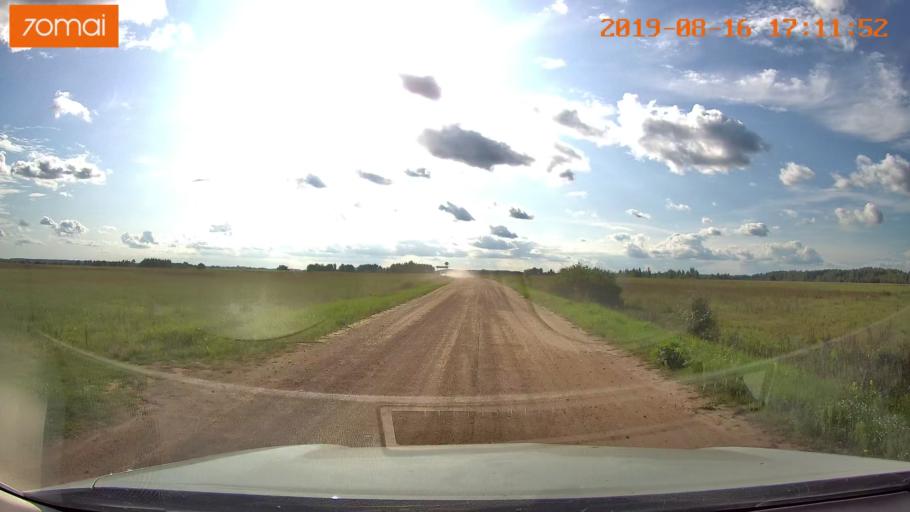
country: BY
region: Mogilev
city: Hlusha
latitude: 53.1966
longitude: 28.9000
